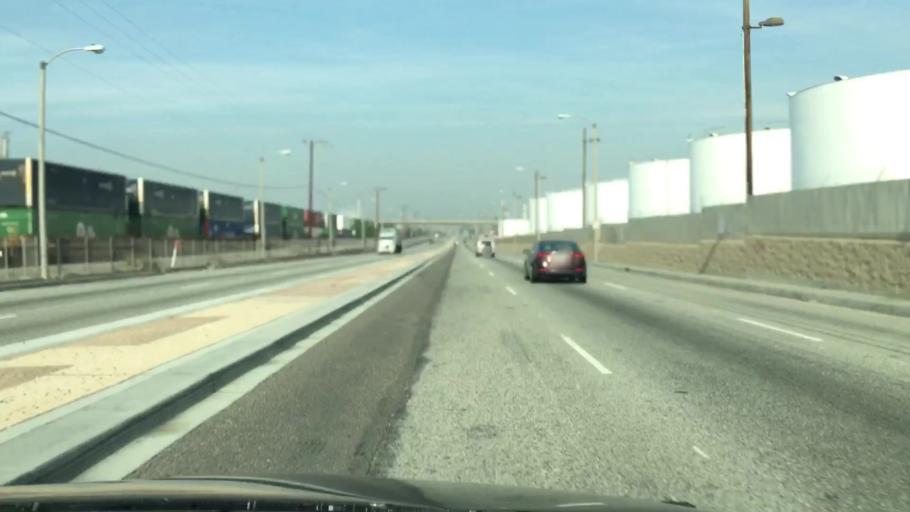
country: US
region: California
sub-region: Los Angeles County
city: Carson
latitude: 33.8024
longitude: -118.2368
